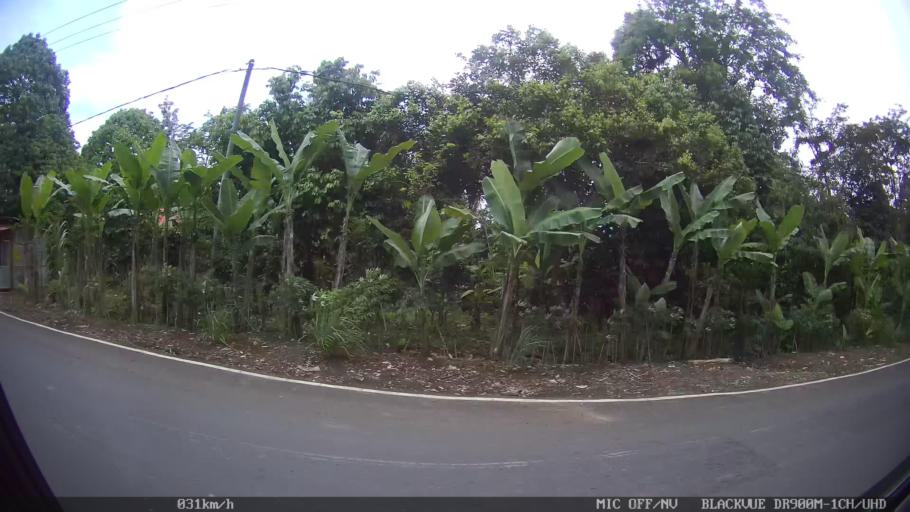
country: ID
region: Lampung
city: Bandarlampung
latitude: -5.4328
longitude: 105.2121
